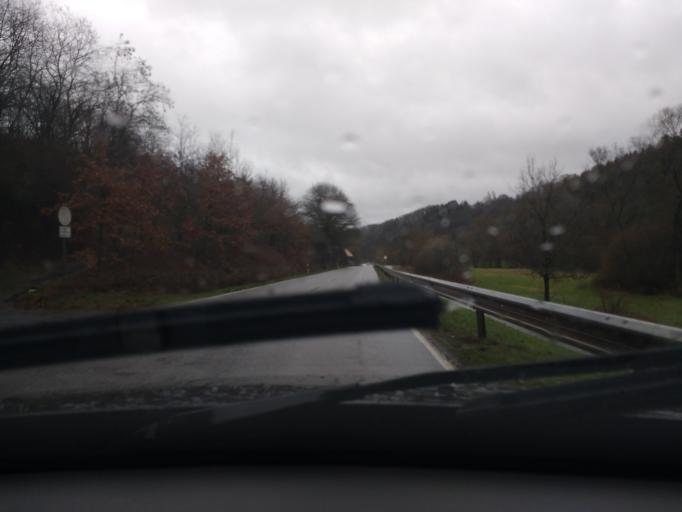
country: DE
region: Rheinland-Pfalz
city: Irsch
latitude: 49.7357
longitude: 6.6782
